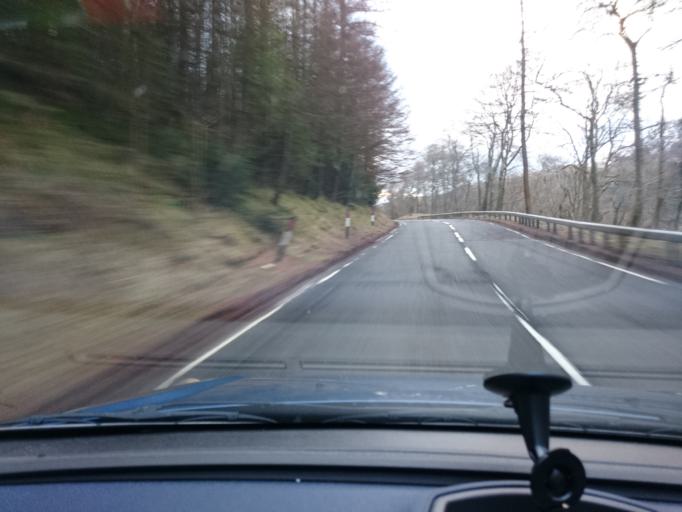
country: GB
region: Scotland
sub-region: Stirling
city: Callander
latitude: 56.2744
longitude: -4.2823
